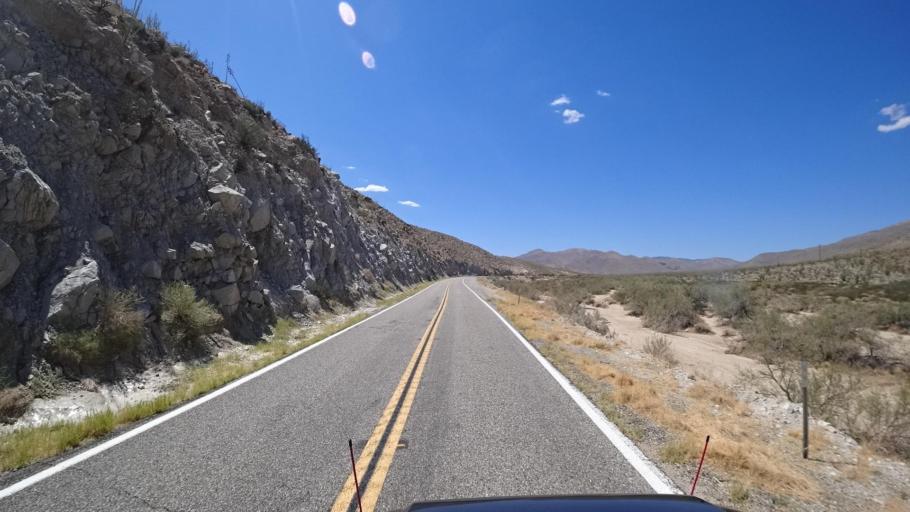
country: US
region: California
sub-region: San Diego County
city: Borrego Springs
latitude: 33.1368
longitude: -116.3759
